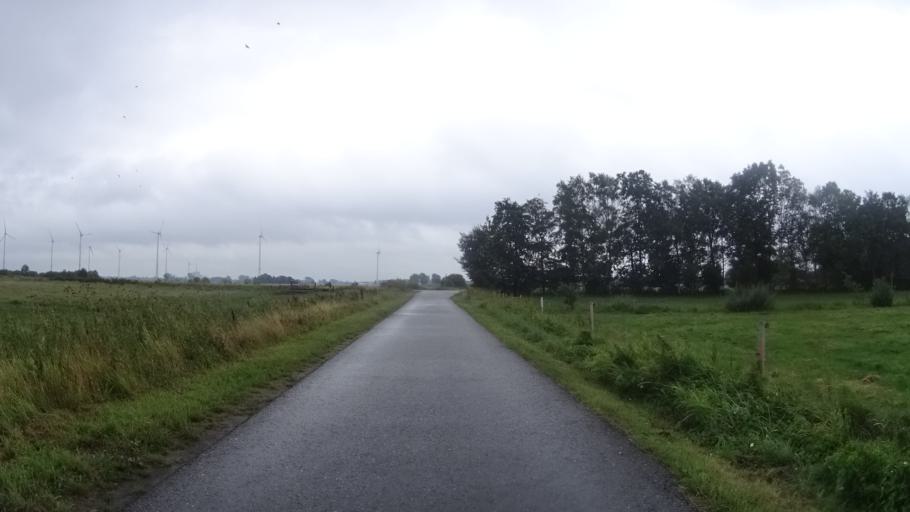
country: DE
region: Lower Saxony
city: Weener
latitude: 53.1800
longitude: 7.3195
